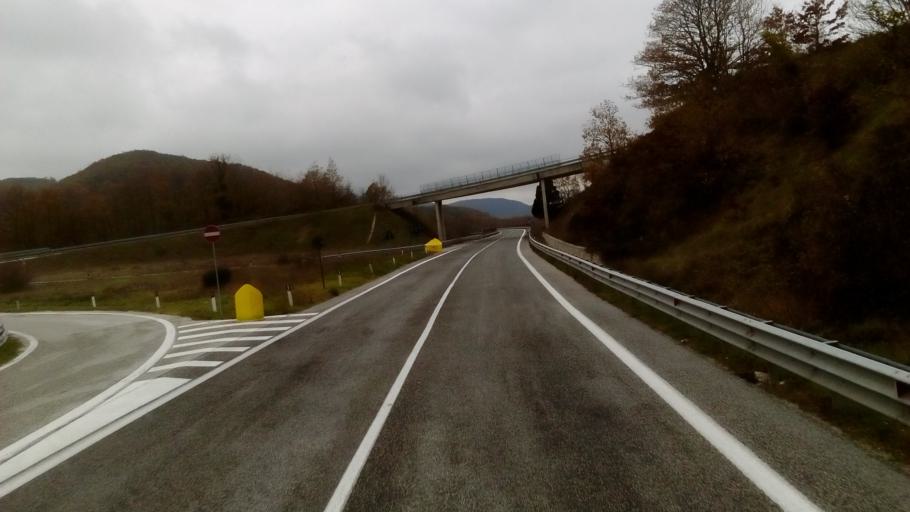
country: IT
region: Molise
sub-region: Provincia di Isernia
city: Chiauci
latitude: 41.6721
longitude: 14.3750
